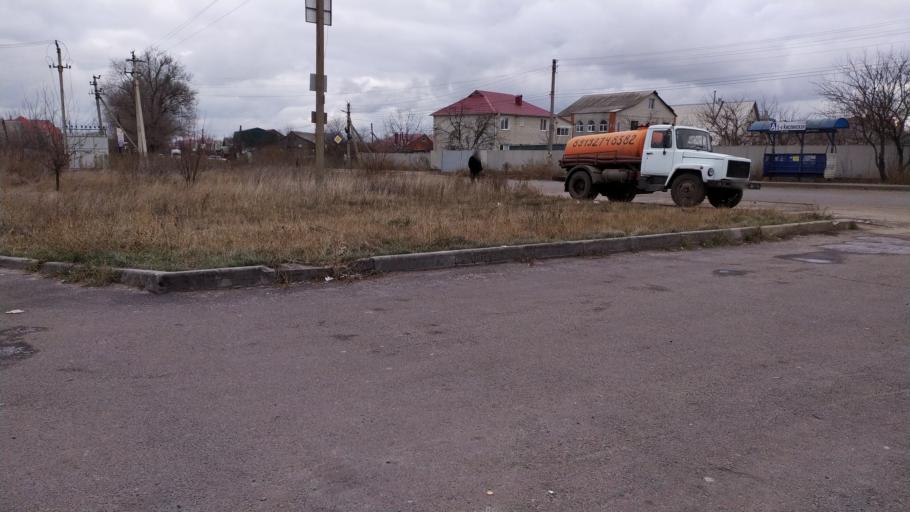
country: RU
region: Kursk
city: Kursk
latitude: 51.6365
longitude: 36.1384
